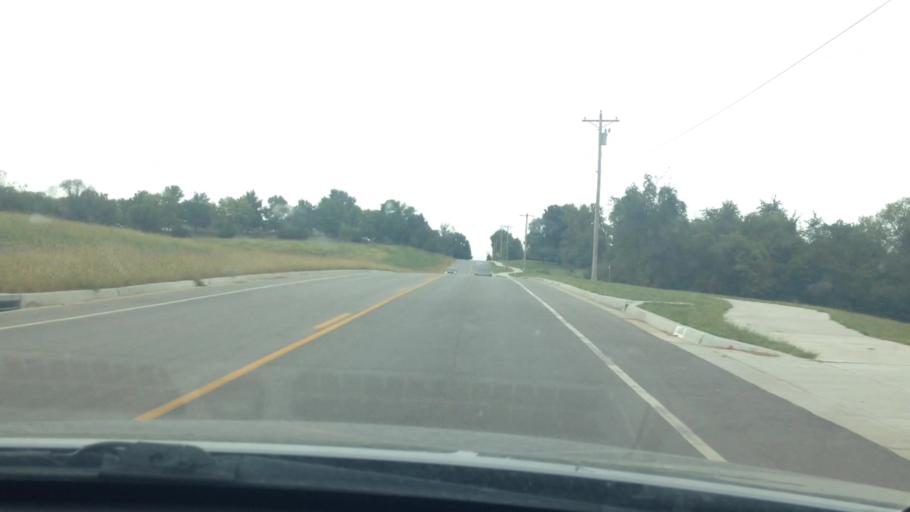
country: US
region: Missouri
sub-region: Platte County
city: Platte City
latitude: 39.3436
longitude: -94.7793
